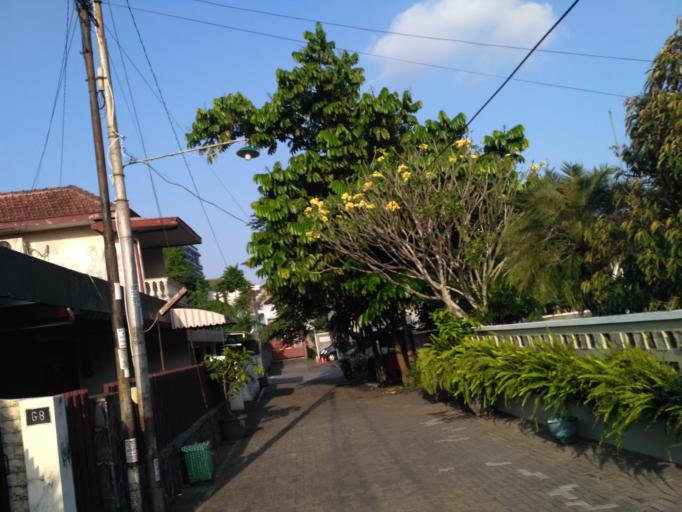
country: ID
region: Daerah Istimewa Yogyakarta
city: Melati
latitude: -7.7579
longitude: 110.3789
